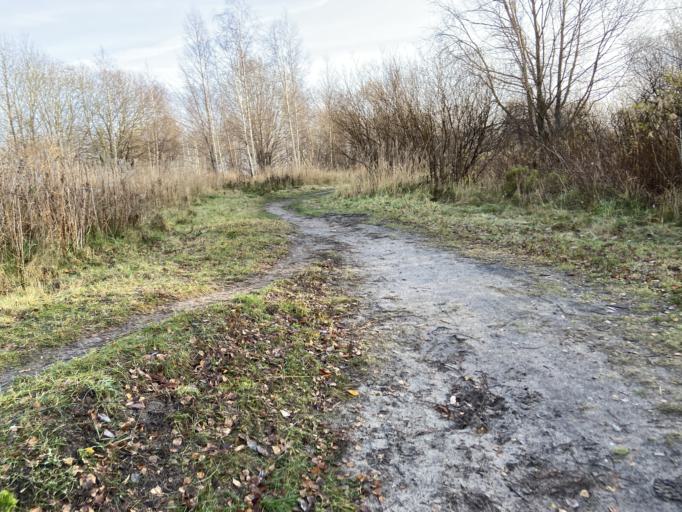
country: EE
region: Harju
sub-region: Tallinna linn
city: Tallinn
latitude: 59.4748
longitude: 24.7198
